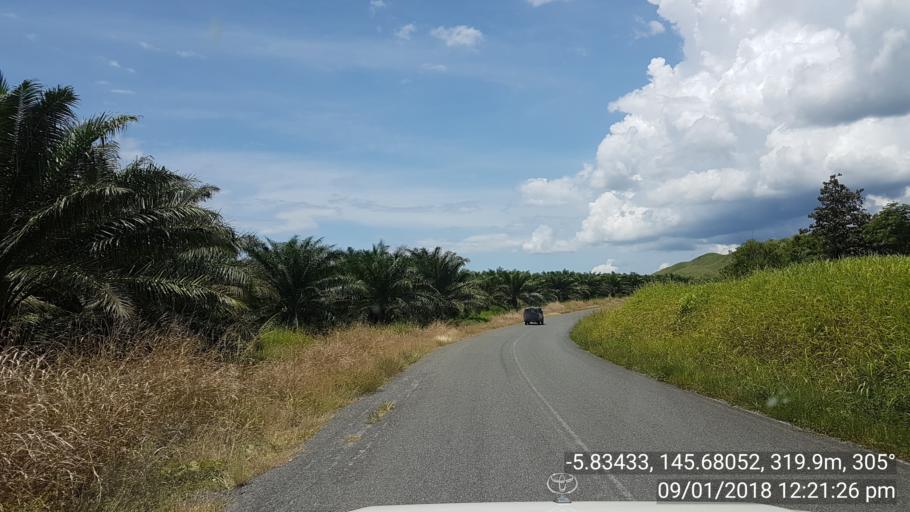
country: PG
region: Eastern Highlands
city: Goroka
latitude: -5.8344
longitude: 145.6806
